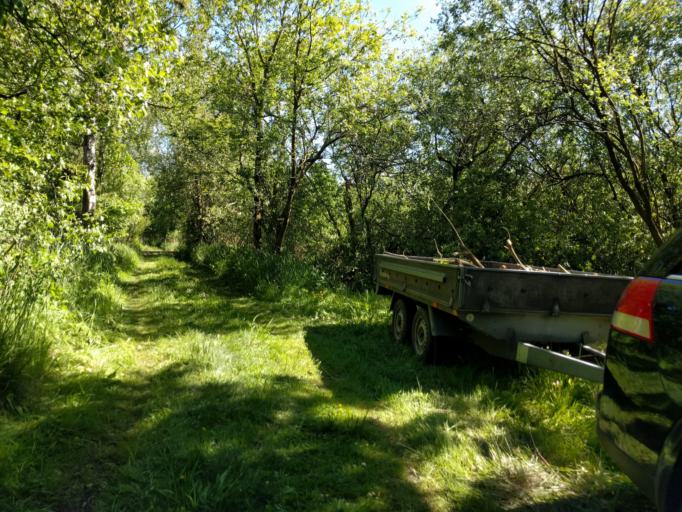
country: DK
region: South Denmark
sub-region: Kerteminde Kommune
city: Langeskov
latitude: 55.3829
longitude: 10.5909
